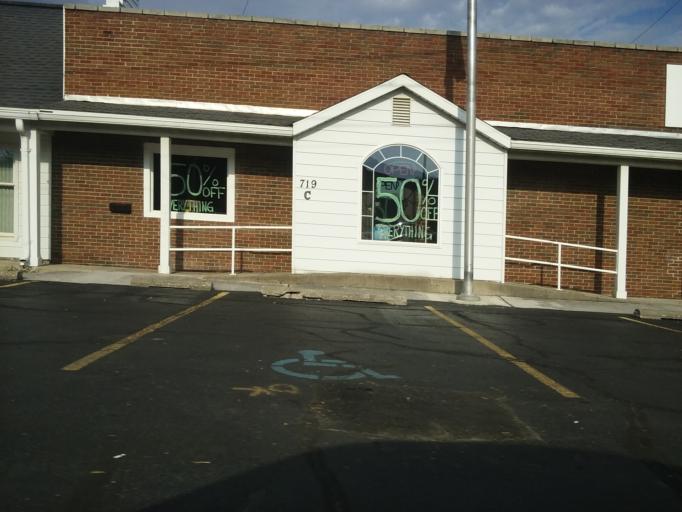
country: US
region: Ohio
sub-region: Wood County
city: Bowling Green
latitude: 41.3643
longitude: -83.6504
